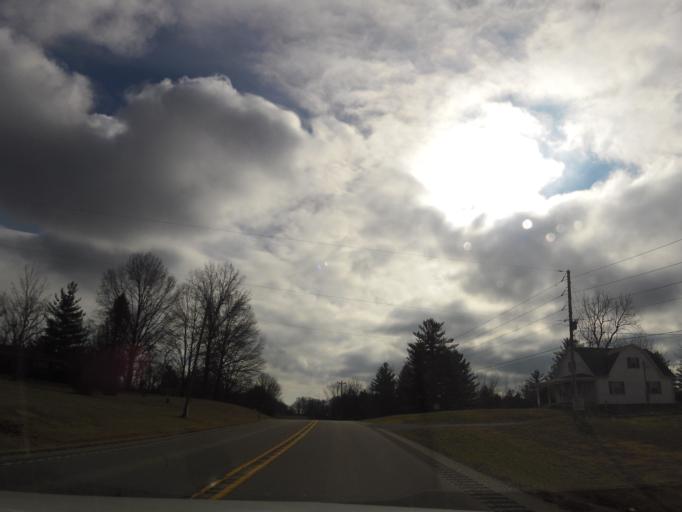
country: US
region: Indiana
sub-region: Jennings County
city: North Vernon
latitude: 38.9438
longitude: -85.5751
